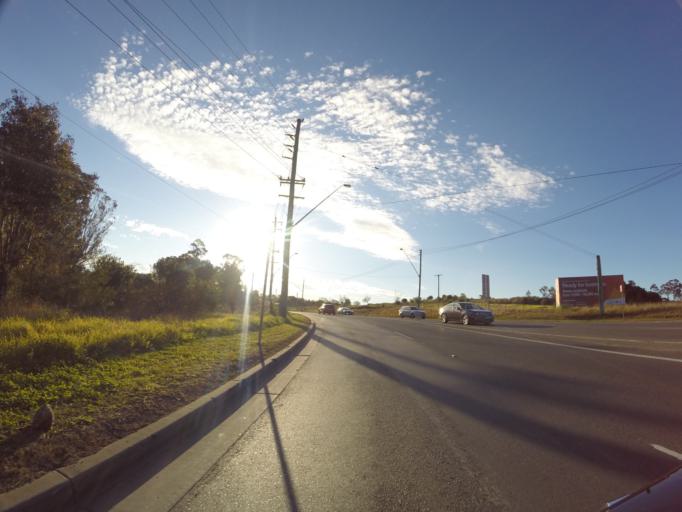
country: AU
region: New South Wales
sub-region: Fairfield
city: Horsley Park
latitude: -33.8487
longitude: 150.8760
